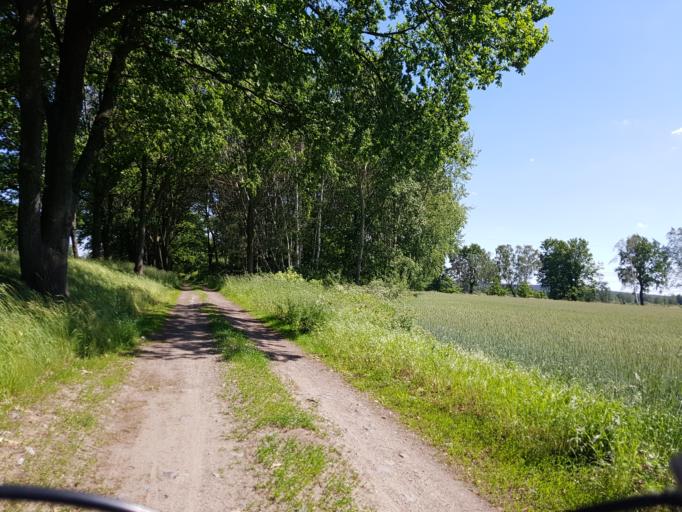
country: DE
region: Brandenburg
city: Merzdorf
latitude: 51.4326
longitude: 13.5408
